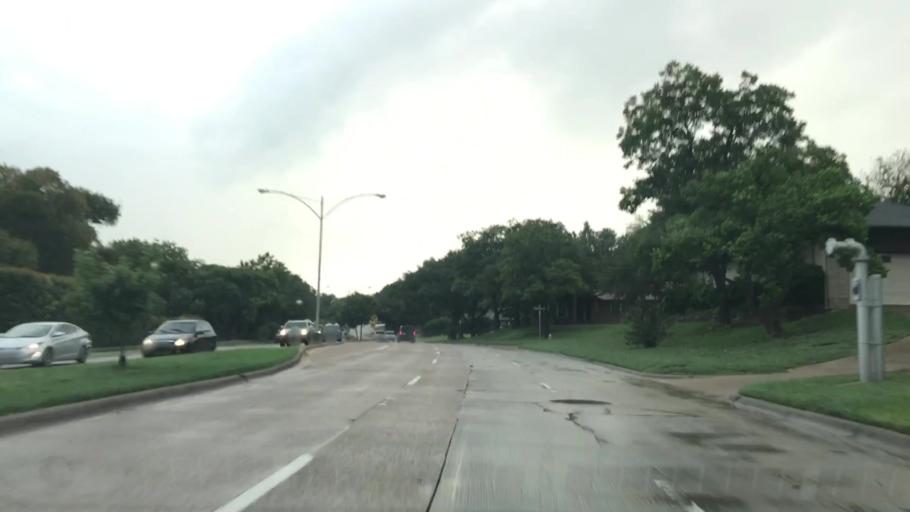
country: US
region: Texas
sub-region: Dallas County
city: University Park
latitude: 32.8962
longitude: -96.7760
